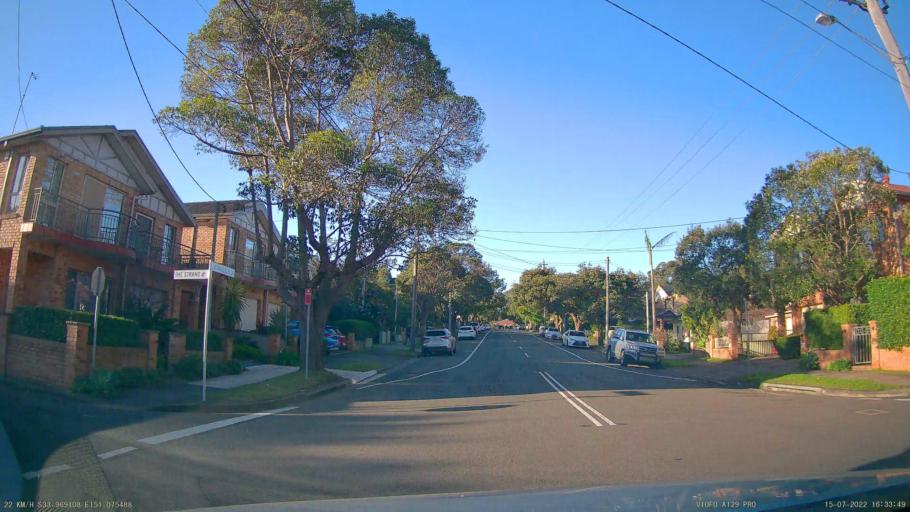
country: AU
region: New South Wales
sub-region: Hurstville
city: Penshurst
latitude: -33.9690
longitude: 151.0757
